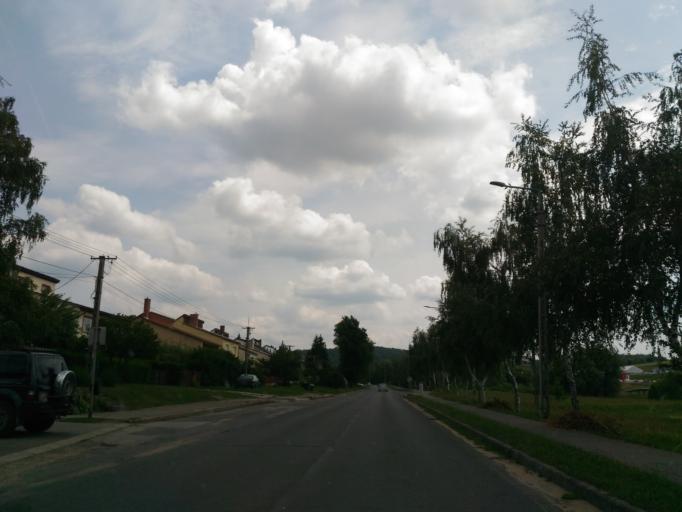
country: HU
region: Baranya
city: Komlo
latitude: 46.1906
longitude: 18.2353
